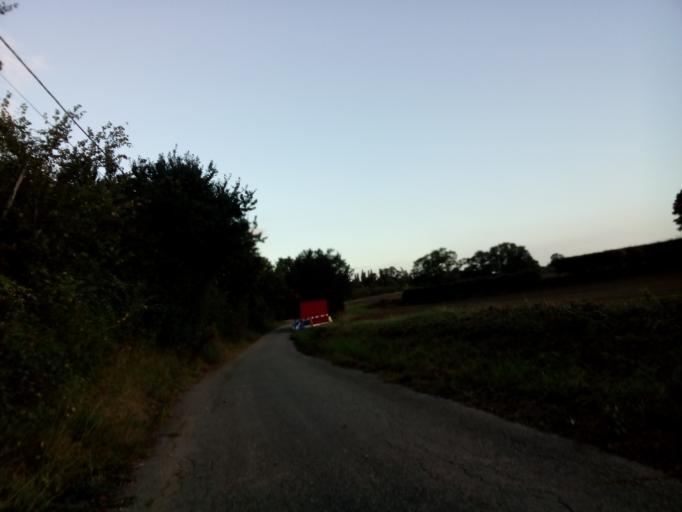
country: GB
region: England
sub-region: Suffolk
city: Bramford
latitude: 52.0562
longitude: 1.1048
